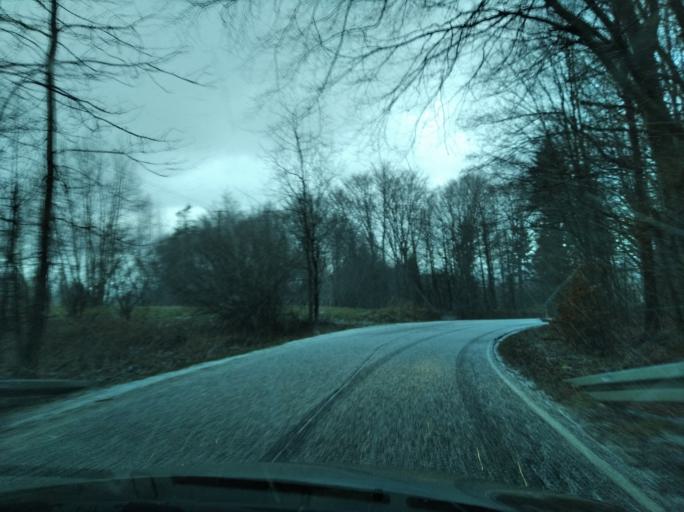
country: PL
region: Subcarpathian Voivodeship
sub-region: Powiat rzeszowski
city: Hyzne
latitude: 49.9430
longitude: 22.1900
